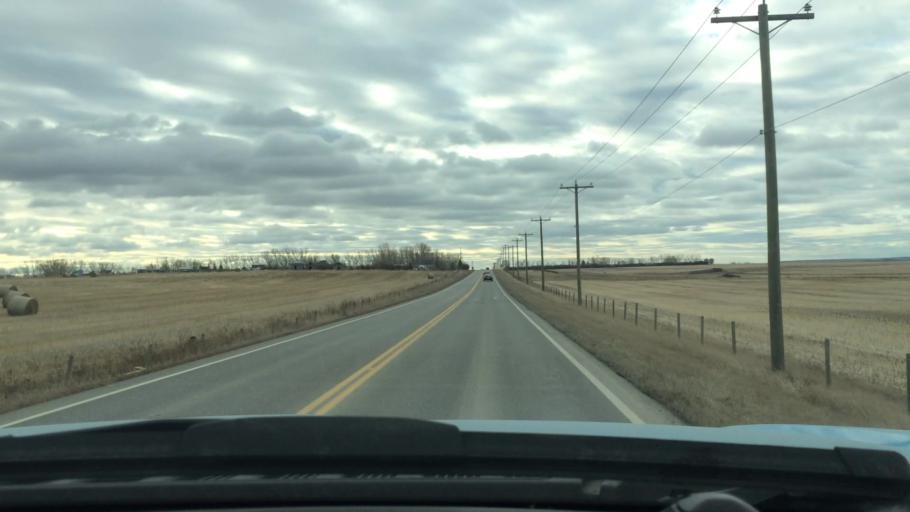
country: CA
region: Alberta
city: Airdrie
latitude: 51.2374
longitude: -114.0250
